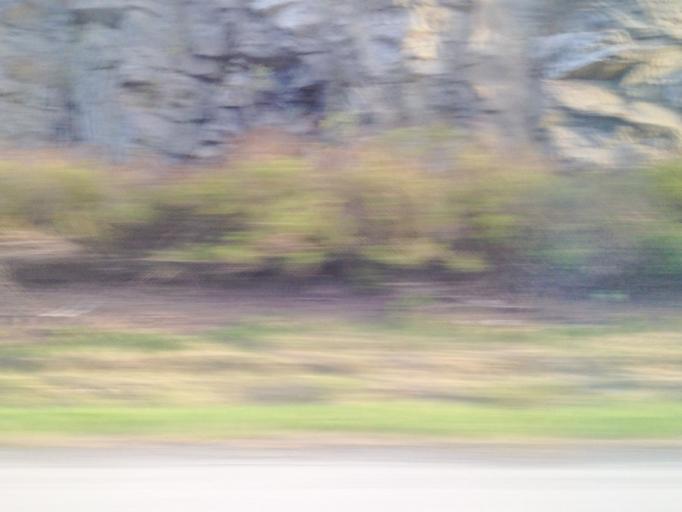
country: FI
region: Pirkanmaa
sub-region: Etelae-Pirkanmaa
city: Akaa
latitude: 61.1771
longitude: 23.9098
